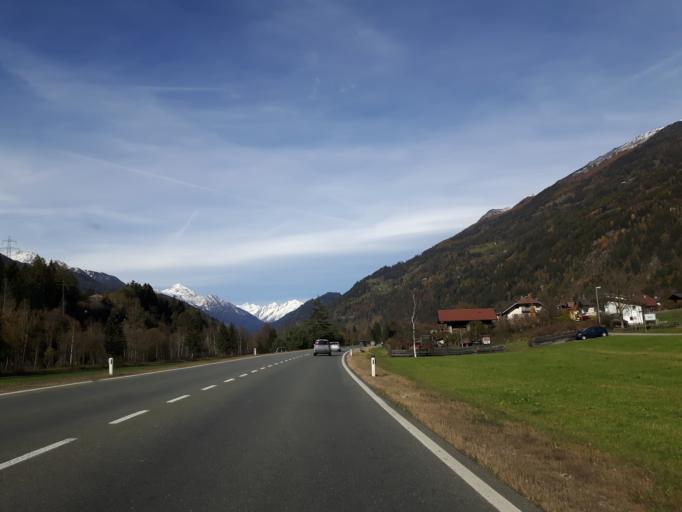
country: AT
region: Tyrol
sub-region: Politischer Bezirk Lienz
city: Ainet
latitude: 46.8611
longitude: 12.6904
